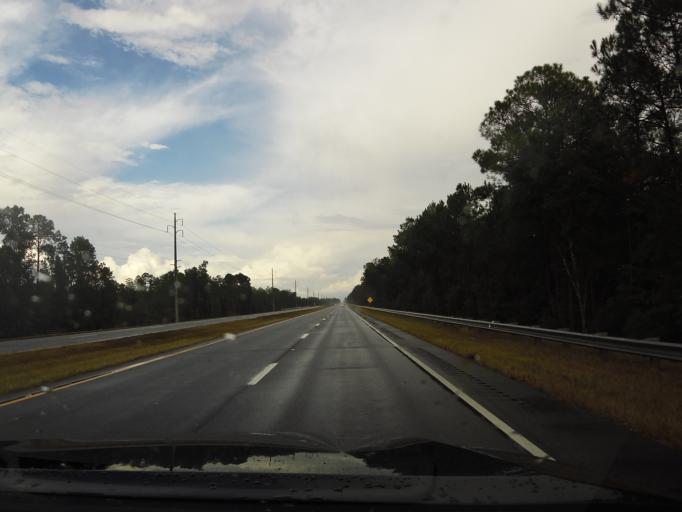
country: US
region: Georgia
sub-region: Long County
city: Ludowici
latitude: 31.6992
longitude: -81.7723
